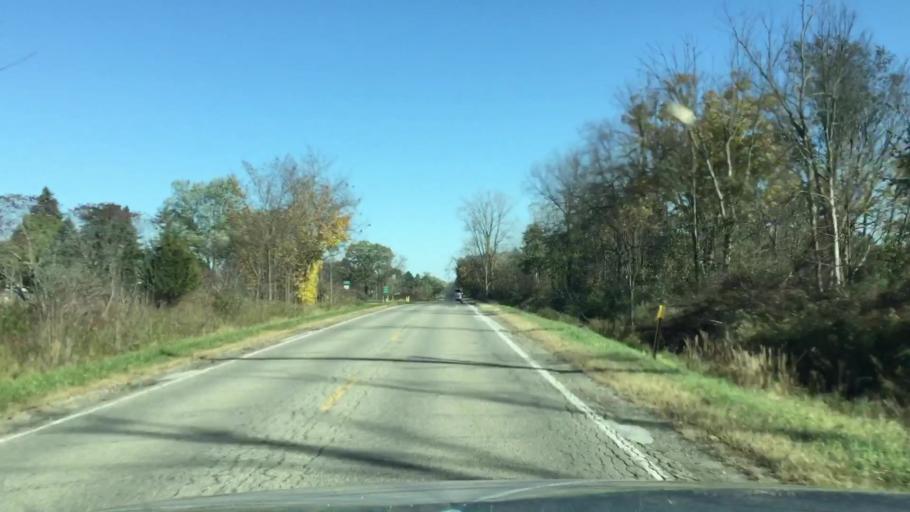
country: US
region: Michigan
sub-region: Lapeer County
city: Lapeer
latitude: 43.0720
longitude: -83.3398
